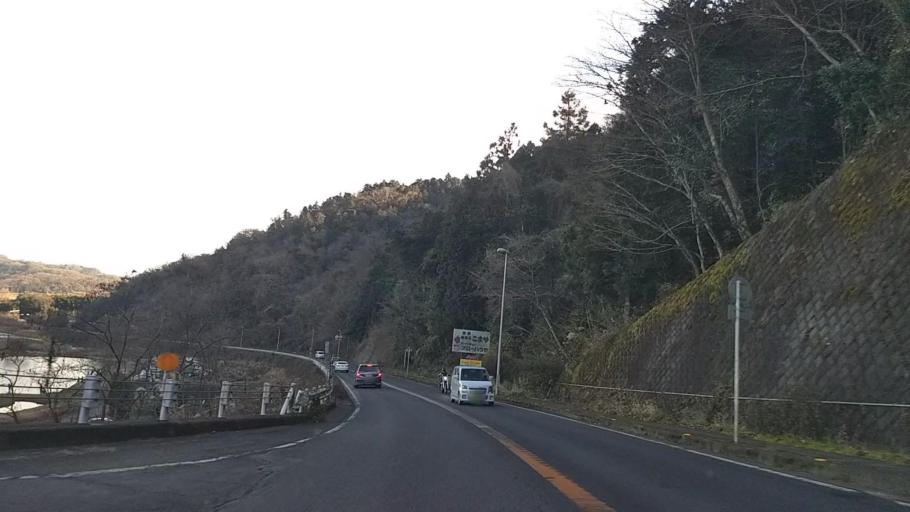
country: JP
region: Kanagawa
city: Zama
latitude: 35.5244
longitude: 139.2819
